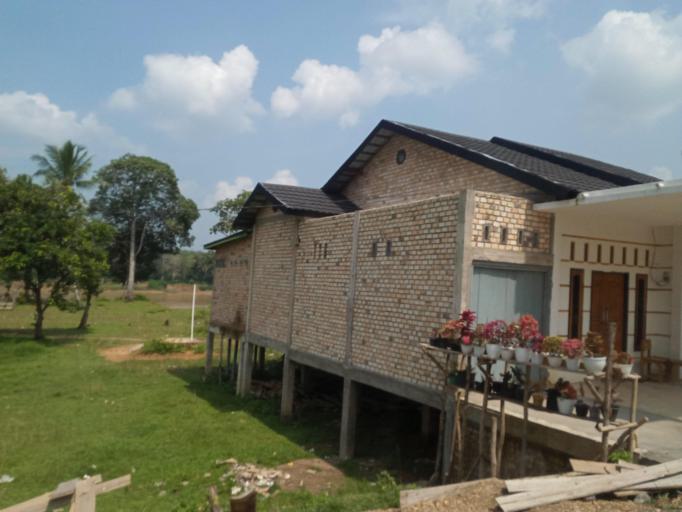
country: ID
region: Jambi
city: Mersam
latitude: -1.7064
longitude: 102.8835
